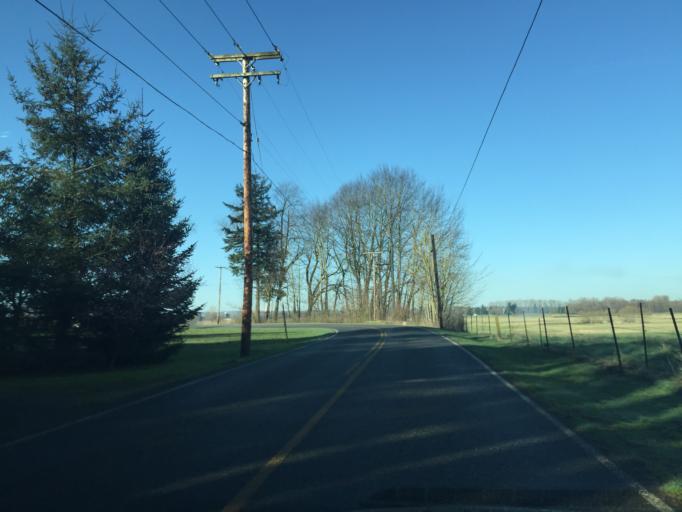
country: US
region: Washington
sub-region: Whatcom County
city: Lynden
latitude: 48.9062
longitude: -122.5116
